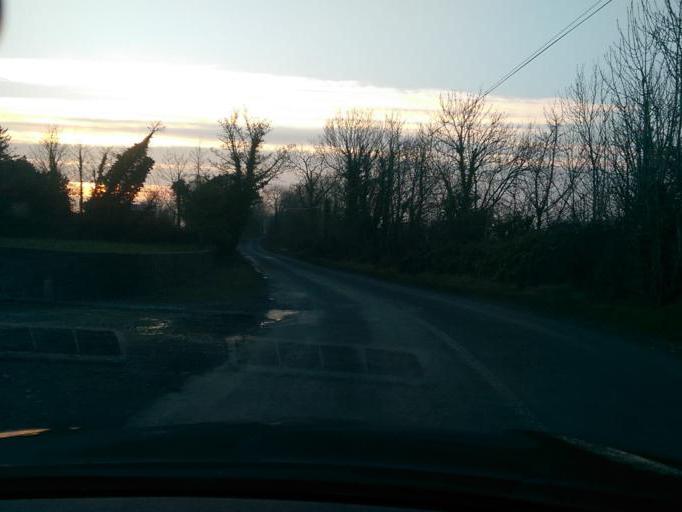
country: IE
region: Connaught
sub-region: County Galway
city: Loughrea
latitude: 53.2349
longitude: -8.6569
